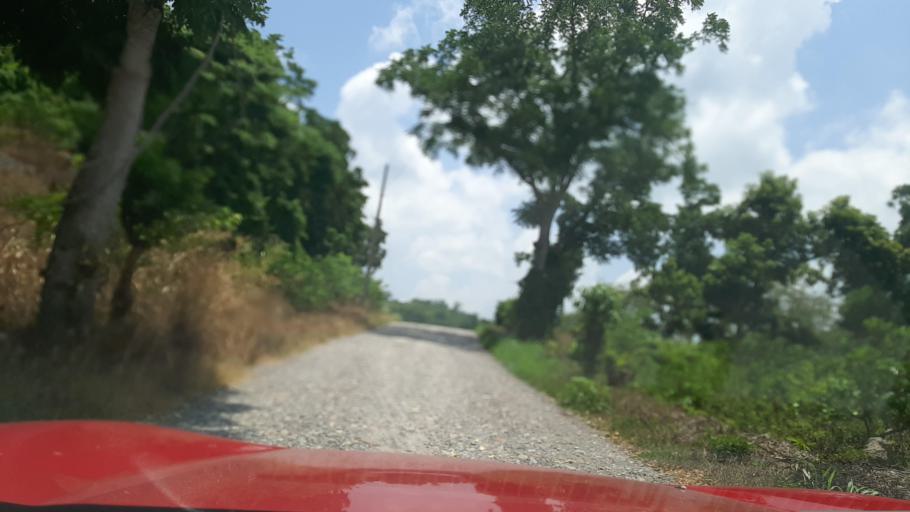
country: MX
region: Veracruz
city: Papantla de Olarte
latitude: 20.4280
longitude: -97.2640
